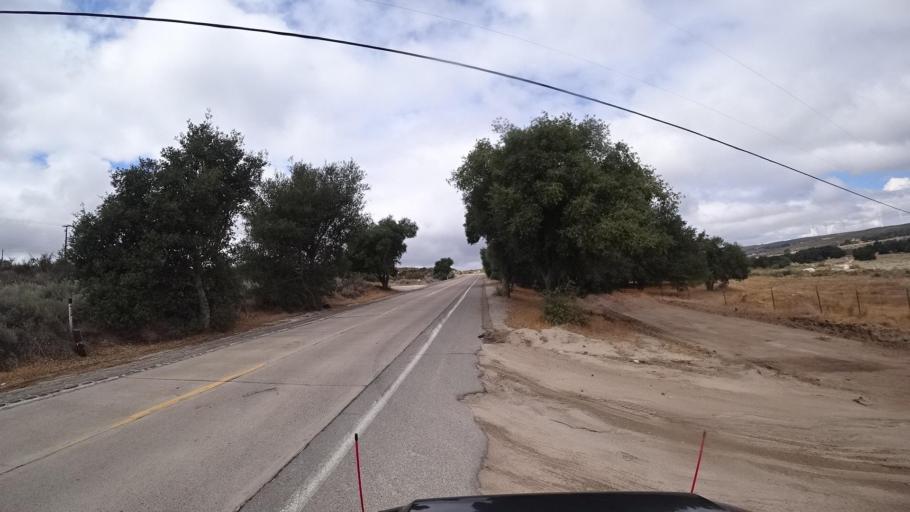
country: US
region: California
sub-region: San Diego County
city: Campo
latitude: 32.6945
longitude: -116.3447
